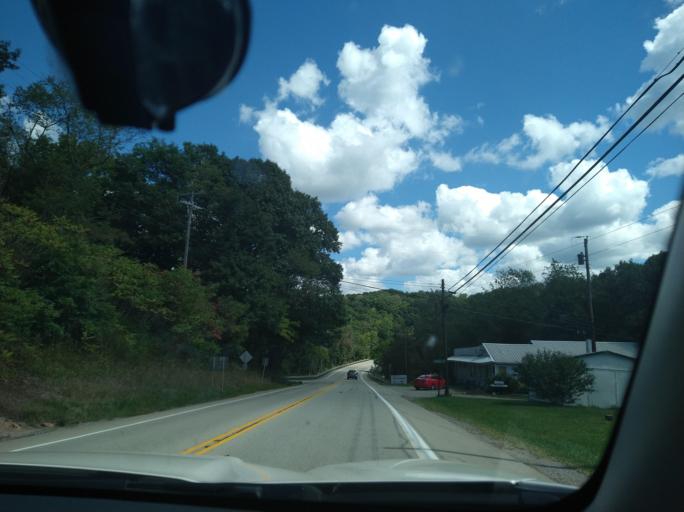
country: US
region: Pennsylvania
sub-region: Fayette County
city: Bear Rocks
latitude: 40.0878
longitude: -79.3375
